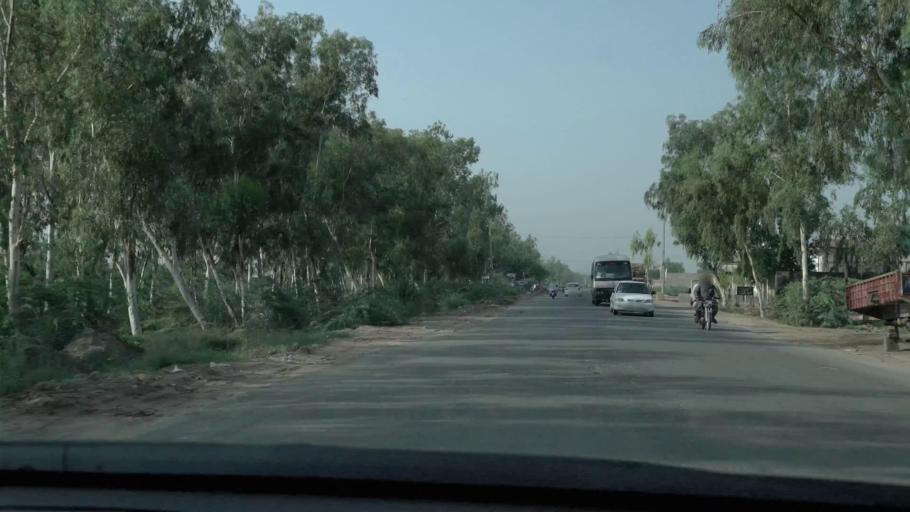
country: PK
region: Punjab
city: Gojra
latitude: 31.1175
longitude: 72.6675
